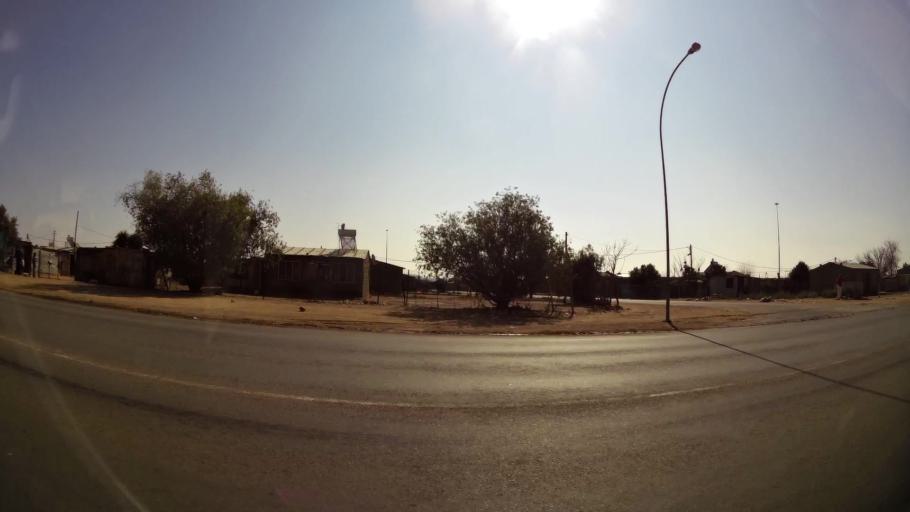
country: ZA
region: Orange Free State
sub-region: Mangaung Metropolitan Municipality
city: Bloemfontein
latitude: -29.1560
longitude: 26.2502
